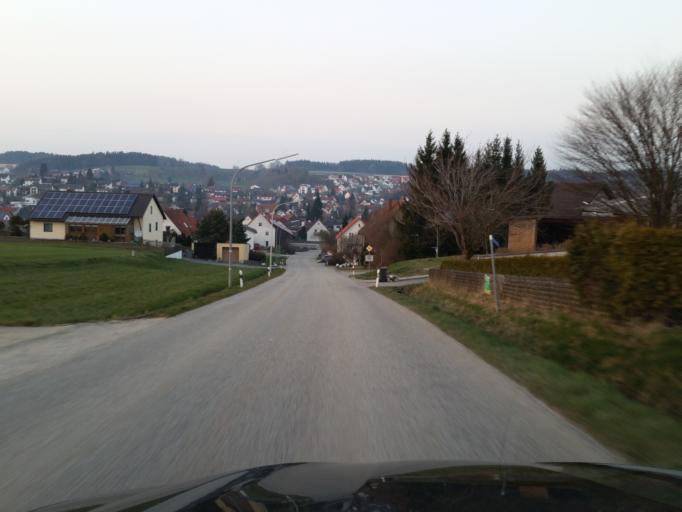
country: DE
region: Bavaria
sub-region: Lower Bavaria
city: Furth
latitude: 48.5848
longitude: 12.0194
